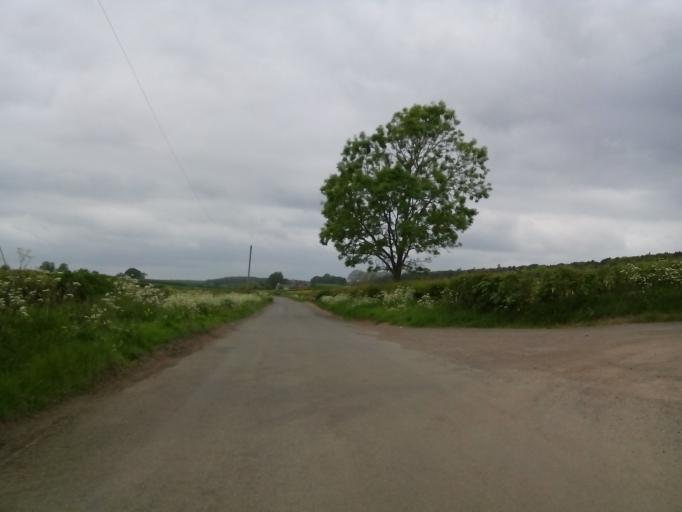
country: GB
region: England
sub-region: Northamptonshire
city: Oundle
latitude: 52.5164
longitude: -0.5110
